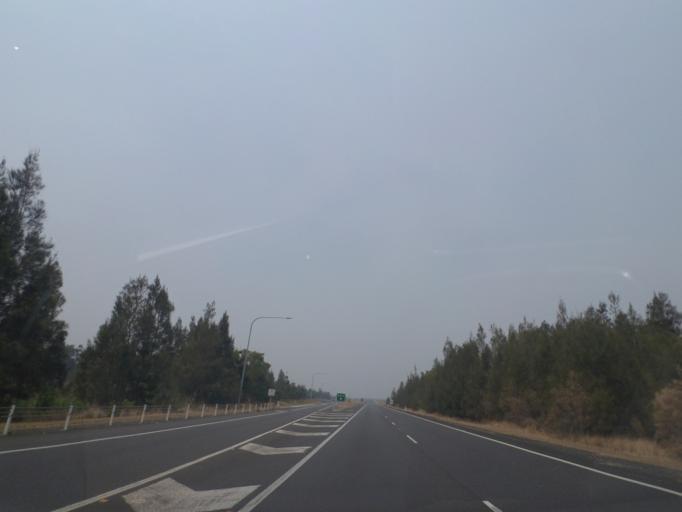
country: AU
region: New South Wales
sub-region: Ballina
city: Ballina
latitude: -28.8636
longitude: 153.5121
